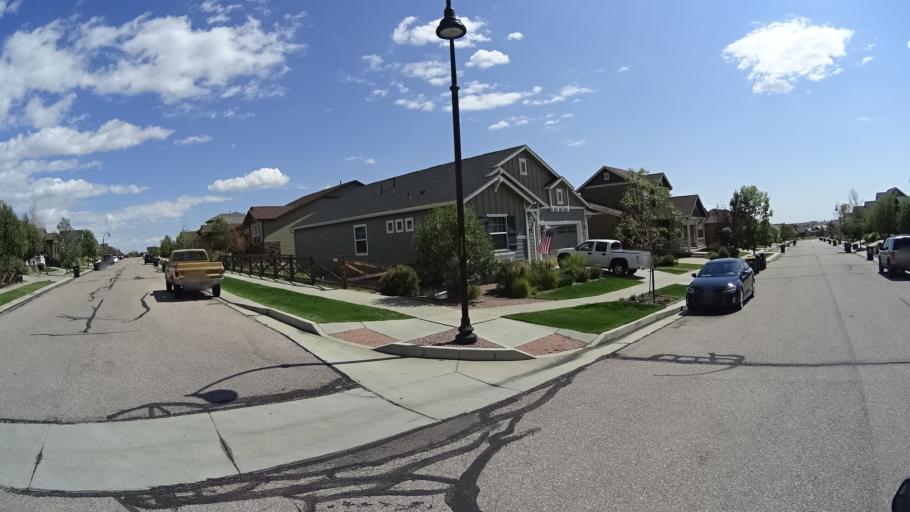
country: US
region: Colorado
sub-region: El Paso County
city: Cimarron Hills
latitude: 38.9307
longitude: -104.6803
